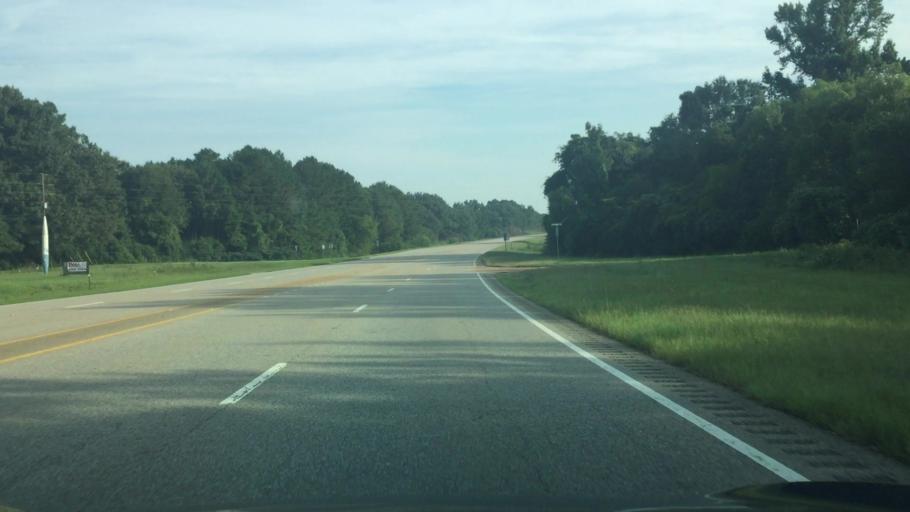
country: US
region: Alabama
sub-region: Covington County
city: Andalusia
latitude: 31.4217
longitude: -86.6109
